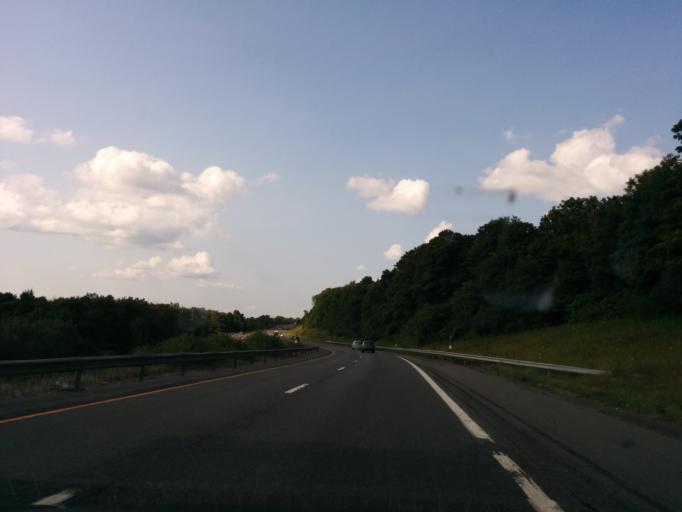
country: US
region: New York
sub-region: Onondaga County
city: Nedrow
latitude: 42.8322
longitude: -76.1233
